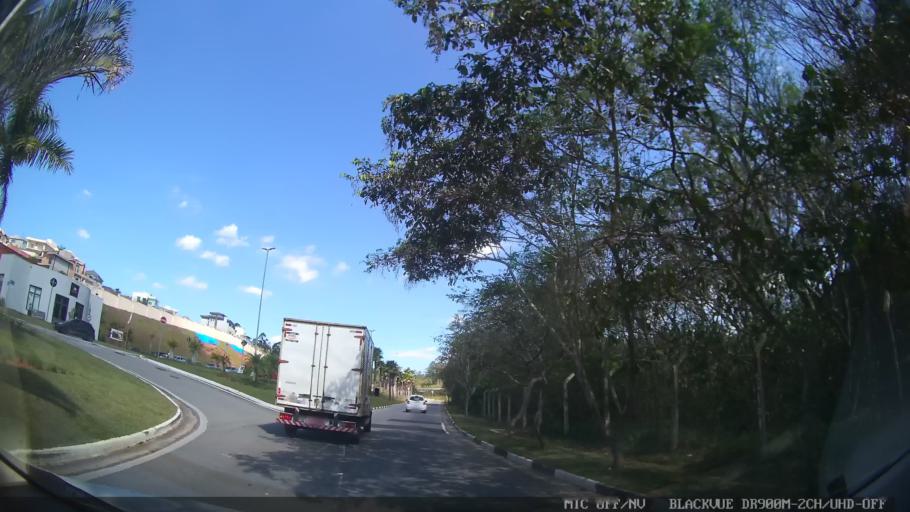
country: BR
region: Sao Paulo
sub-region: Barueri
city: Barueri
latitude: -23.4394
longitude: -46.8328
